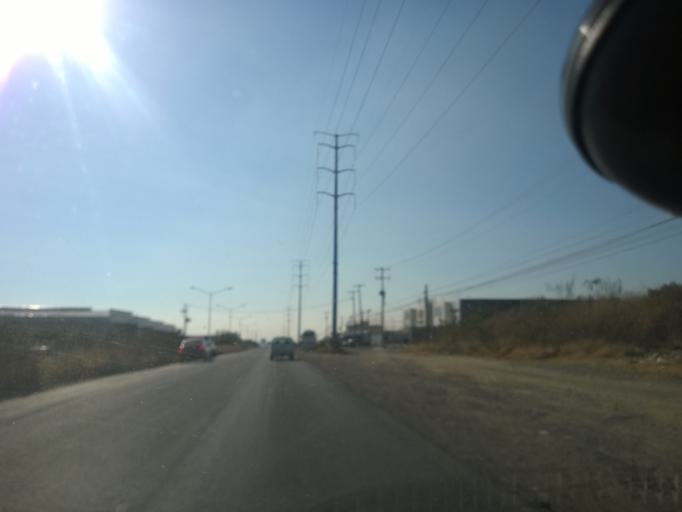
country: MX
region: Guanajuato
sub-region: Leon
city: La Ermita
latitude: 21.1562
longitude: -101.7312
